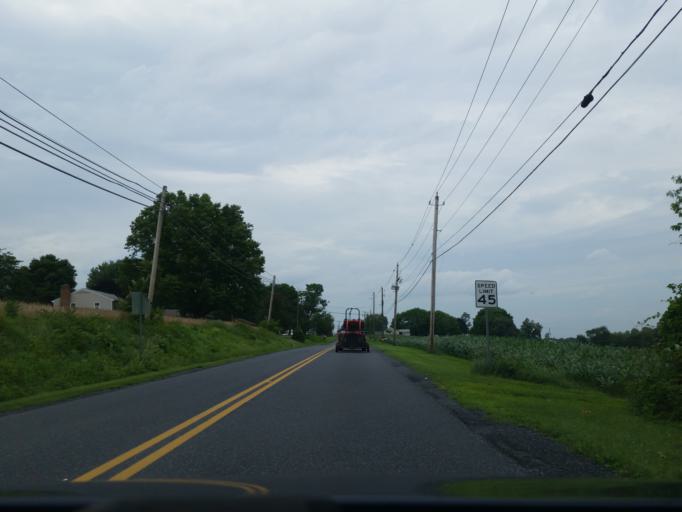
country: US
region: Pennsylvania
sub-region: Lebanon County
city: Jonestown
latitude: 40.4066
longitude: -76.5216
